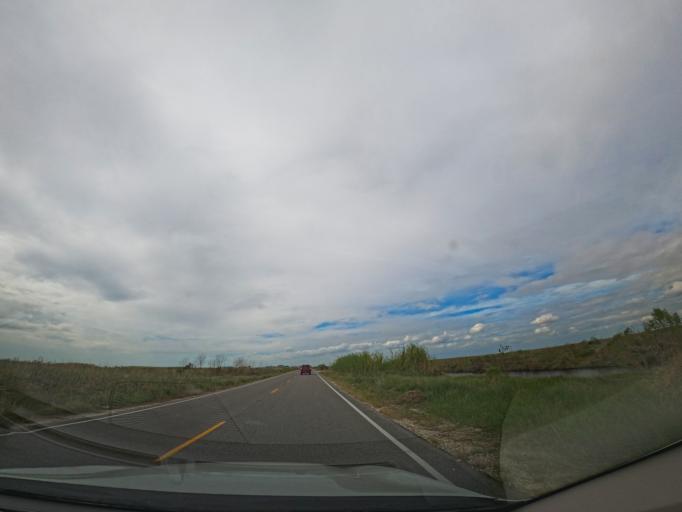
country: US
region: Louisiana
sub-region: Cameron Parish
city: Cameron
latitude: 29.7717
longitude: -93.4392
